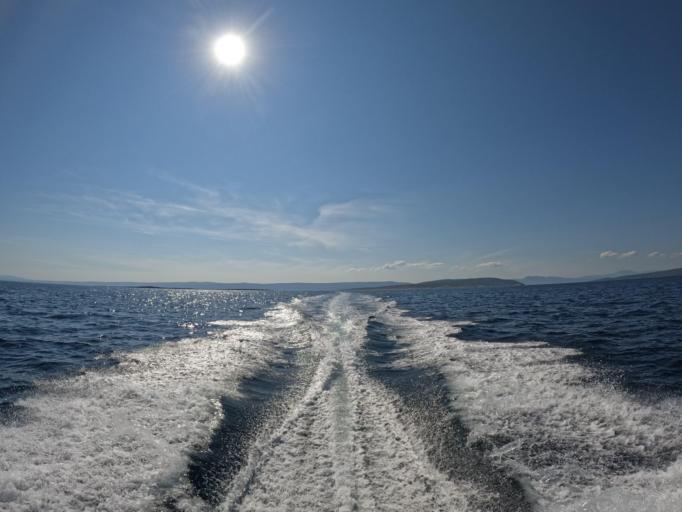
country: HR
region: Primorsko-Goranska
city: Punat
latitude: 44.9541
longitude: 14.5932
